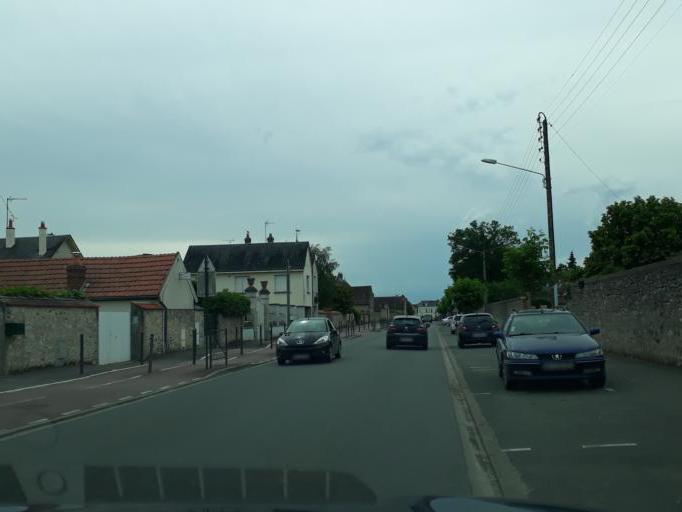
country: FR
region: Centre
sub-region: Departement du Loiret
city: Sully-sur-Loire
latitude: 47.7637
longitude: 2.3836
